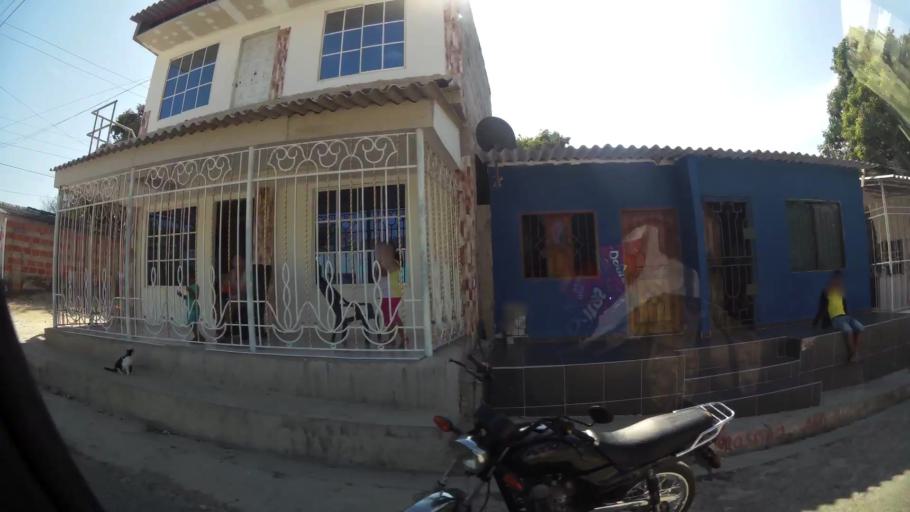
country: CO
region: Atlantico
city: Barranquilla
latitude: 10.9304
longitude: -74.8176
